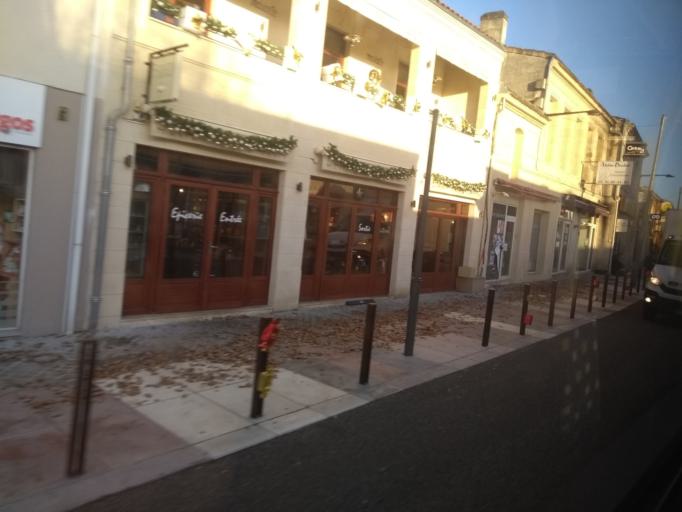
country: FR
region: Aquitaine
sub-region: Departement de la Gironde
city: Gradignan
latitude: 44.7721
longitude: -0.6144
